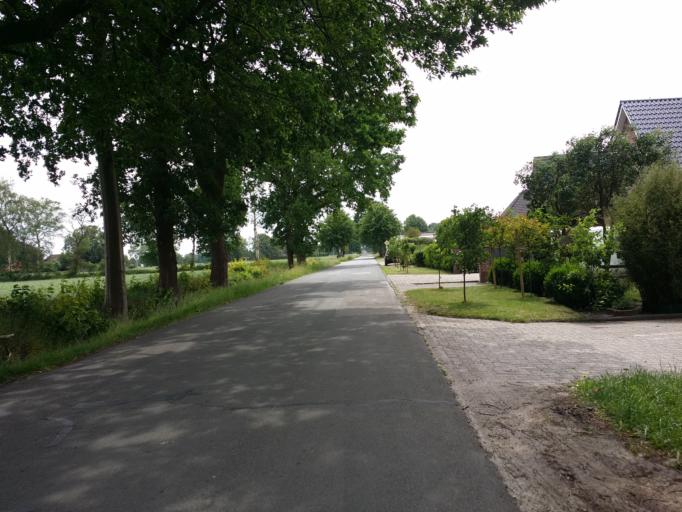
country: DE
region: Lower Saxony
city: Bockhorn
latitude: 53.3384
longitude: 8.0311
